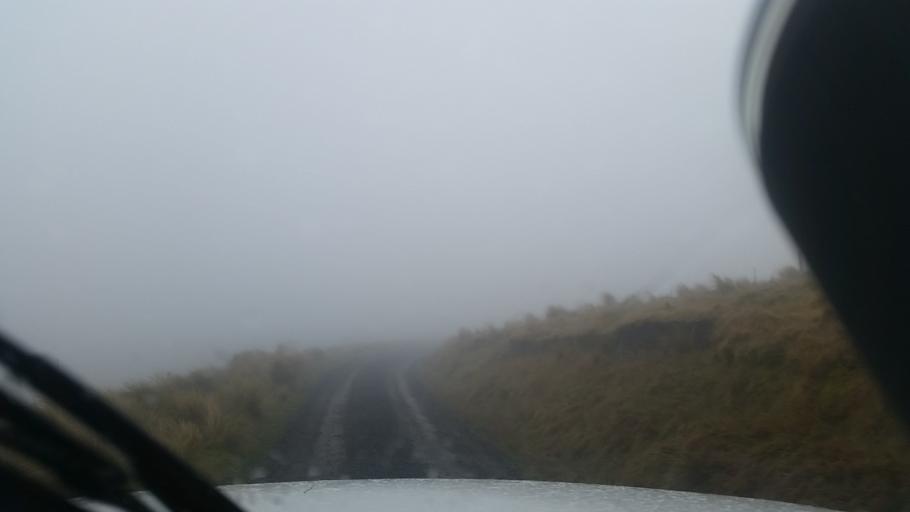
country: NZ
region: Canterbury
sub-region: Christchurch City
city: Christchurch
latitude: -43.8708
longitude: 172.9070
